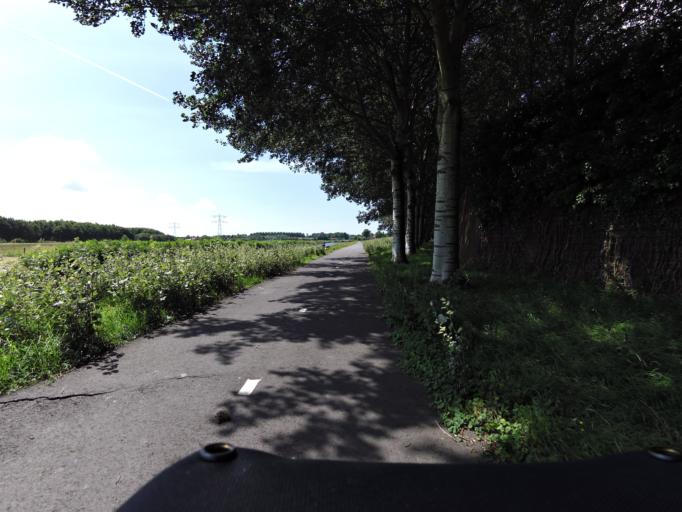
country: NL
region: South Holland
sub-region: Gemeente Albrandswaard
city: Rhoon
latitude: 51.8667
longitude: 4.4185
